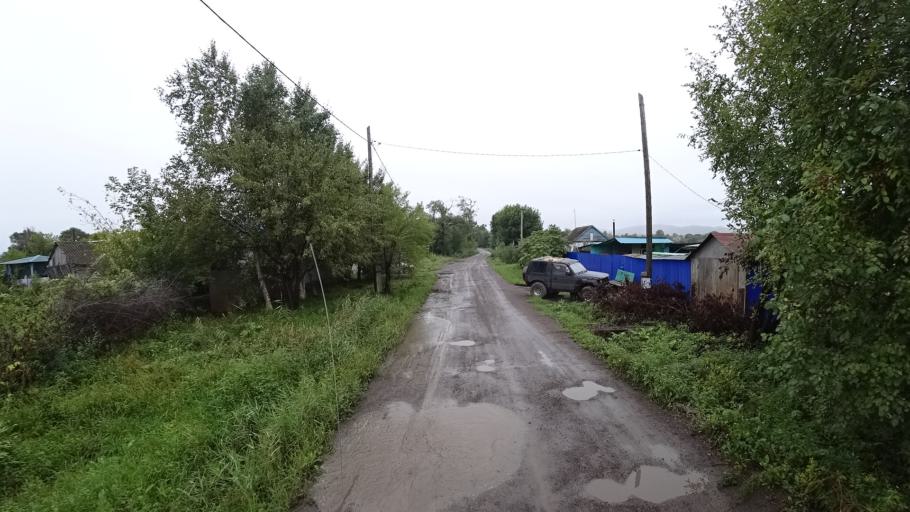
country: RU
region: Primorskiy
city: Monastyrishche
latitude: 44.2001
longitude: 132.4219
